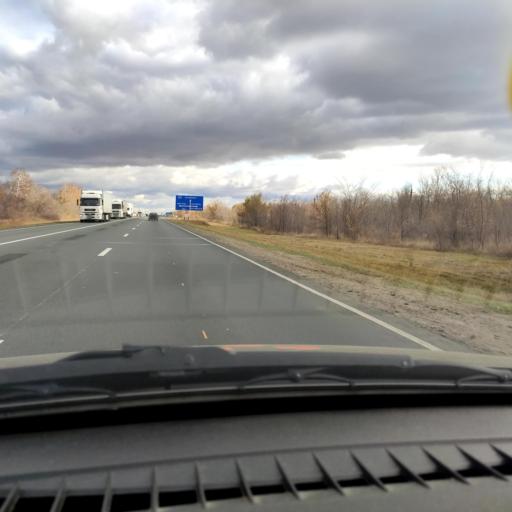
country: RU
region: Samara
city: Syzran'
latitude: 53.2121
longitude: 48.5475
